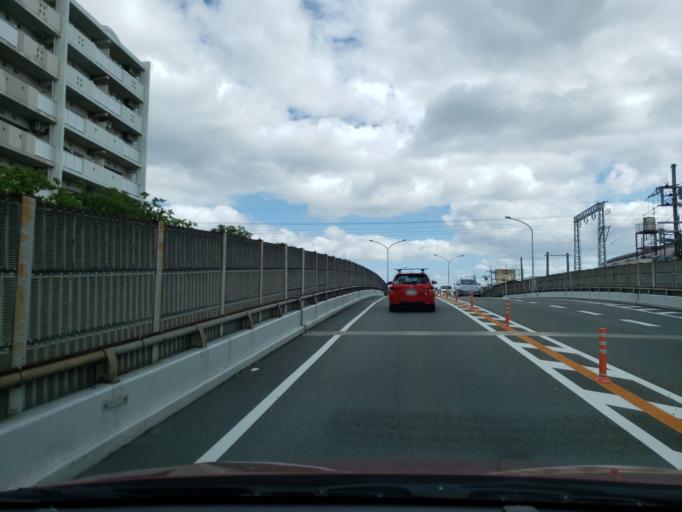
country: JP
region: Osaka
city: Toyonaka
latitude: 34.7578
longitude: 135.4745
